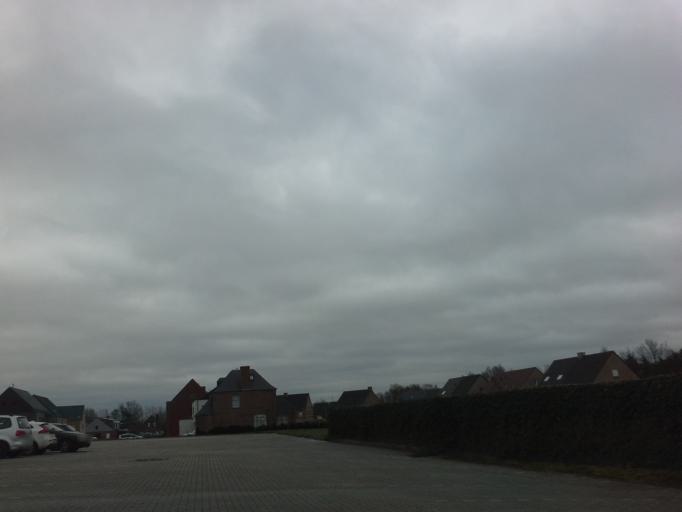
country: BE
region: Flanders
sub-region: Provincie Antwerpen
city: Heist-op-den-Berg
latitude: 51.0673
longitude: 4.7162
